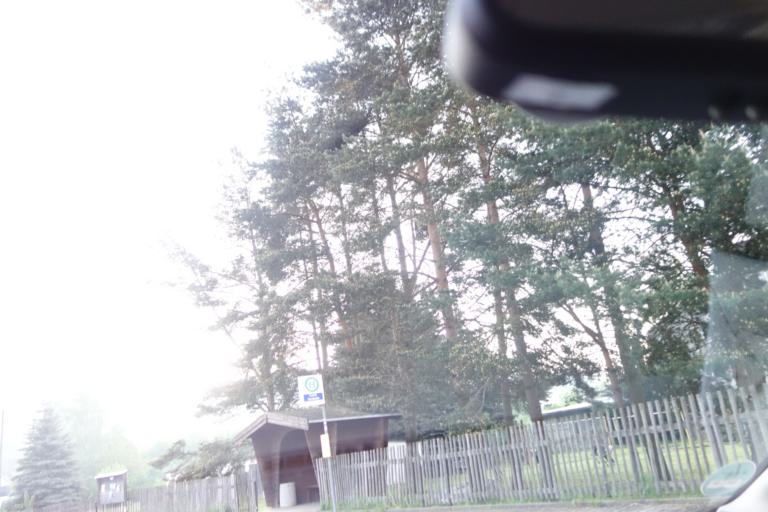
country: DE
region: Saxony
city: Pockau
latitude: 50.7028
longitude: 13.2328
